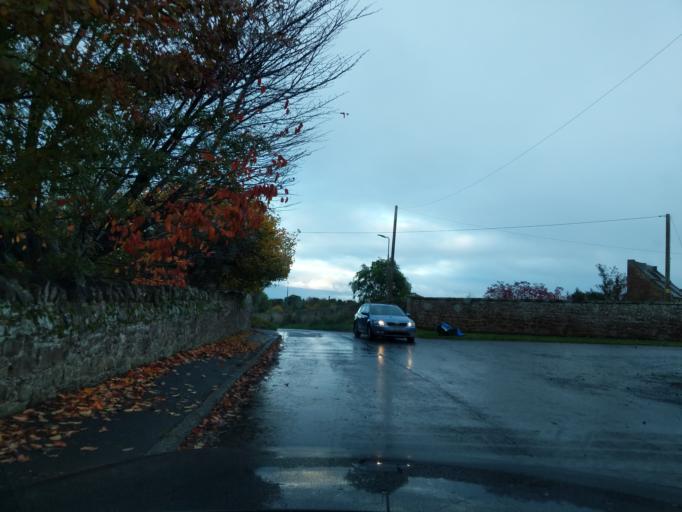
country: GB
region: Scotland
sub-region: East Lothian
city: Dunbar
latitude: 55.9720
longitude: -2.5235
